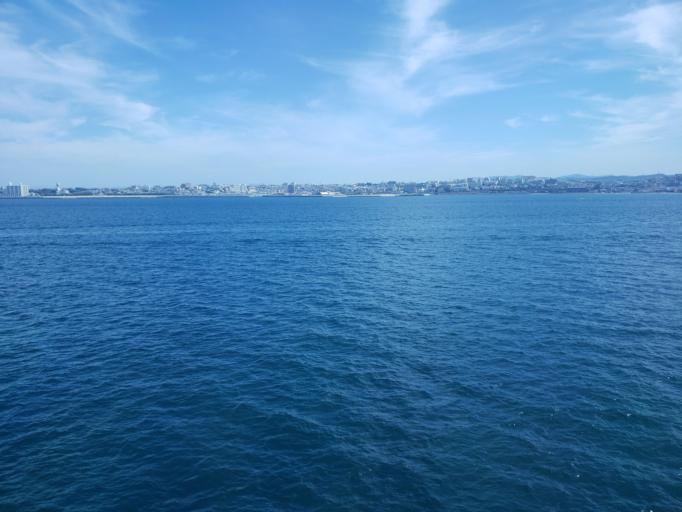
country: JP
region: Hyogo
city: Akashi
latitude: 34.6251
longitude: 135.0103
